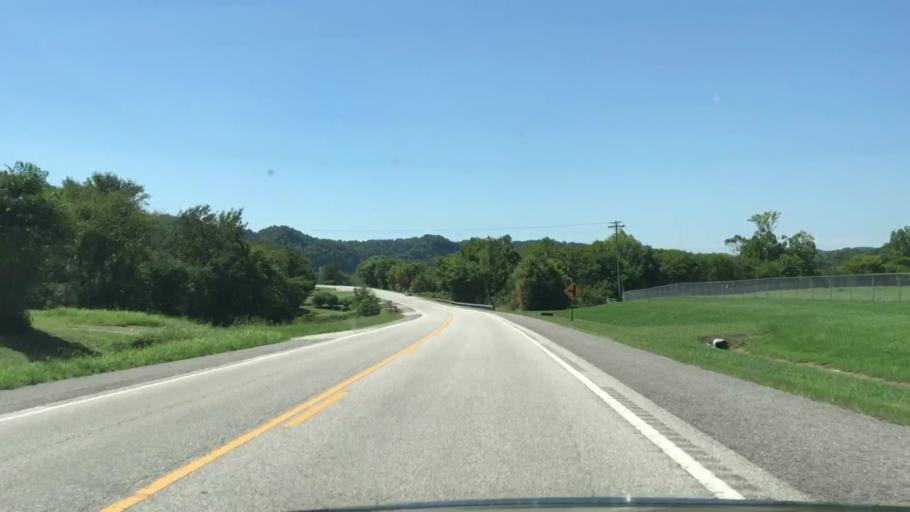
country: US
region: Tennessee
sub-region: Clay County
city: Celina
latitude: 36.5218
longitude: -85.5311
